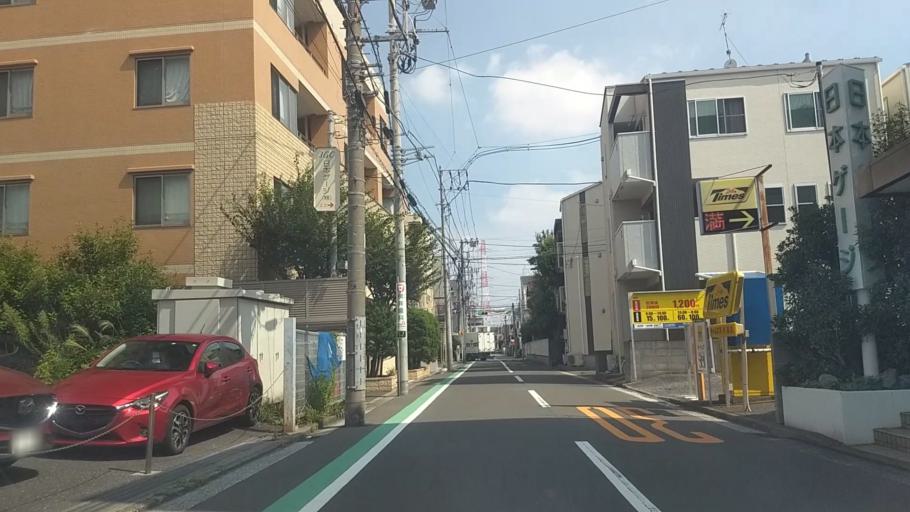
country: JP
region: Kanagawa
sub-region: Kawasaki-shi
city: Kawasaki
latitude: 35.5255
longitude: 139.6839
